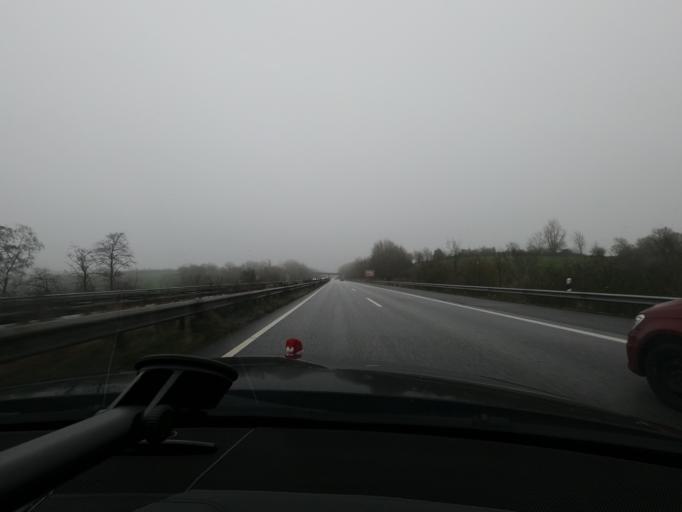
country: DE
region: Schleswig-Holstein
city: Dannewerk
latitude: 54.5002
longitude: 9.5110
